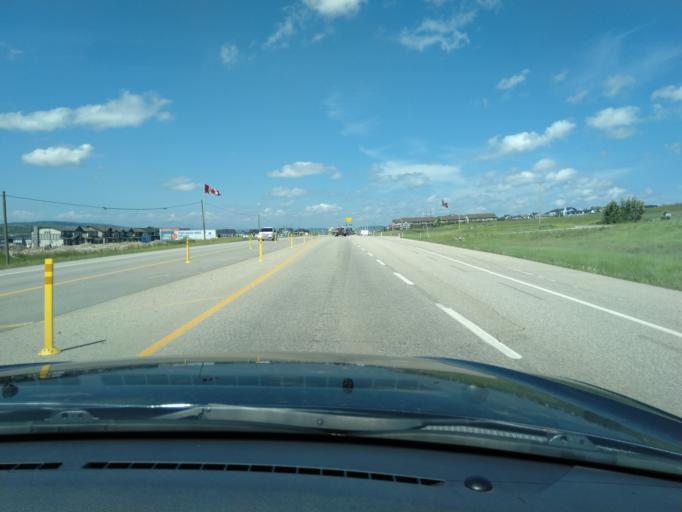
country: CA
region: Alberta
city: Cochrane
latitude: 51.2023
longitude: -114.4992
